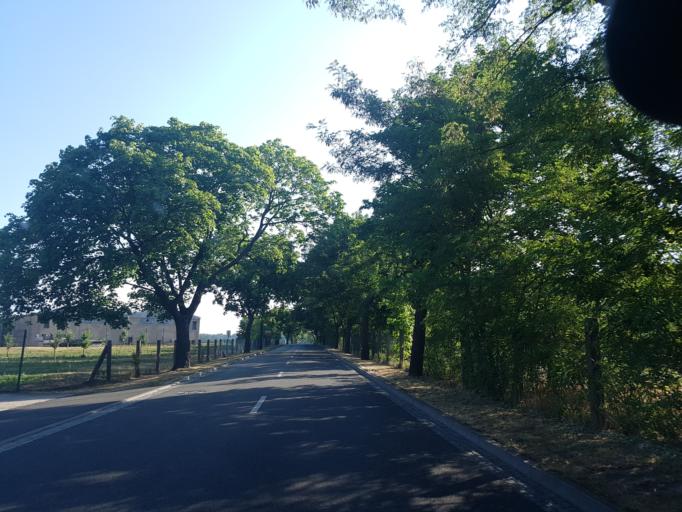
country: DE
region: Saxony-Anhalt
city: Seyda
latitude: 51.8848
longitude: 12.9215
